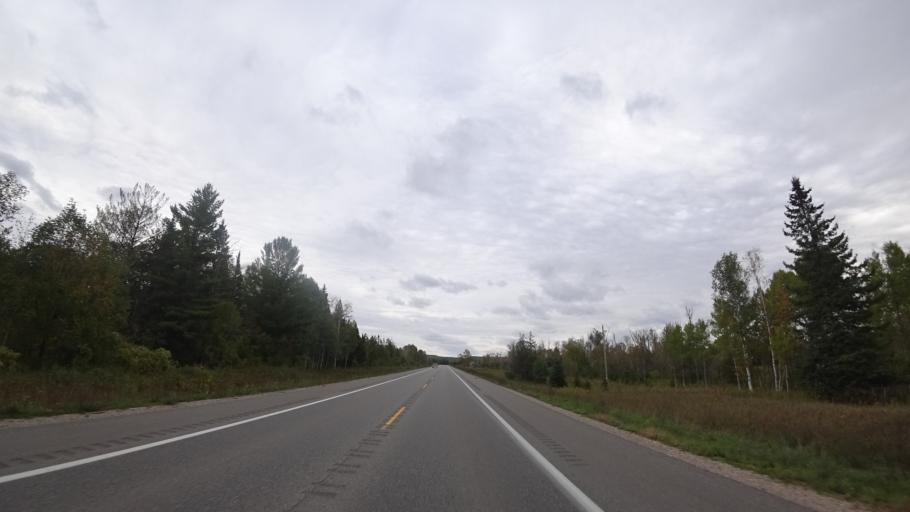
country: US
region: Michigan
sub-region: Charlevoix County
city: Boyne City
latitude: 45.1427
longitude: -84.9073
